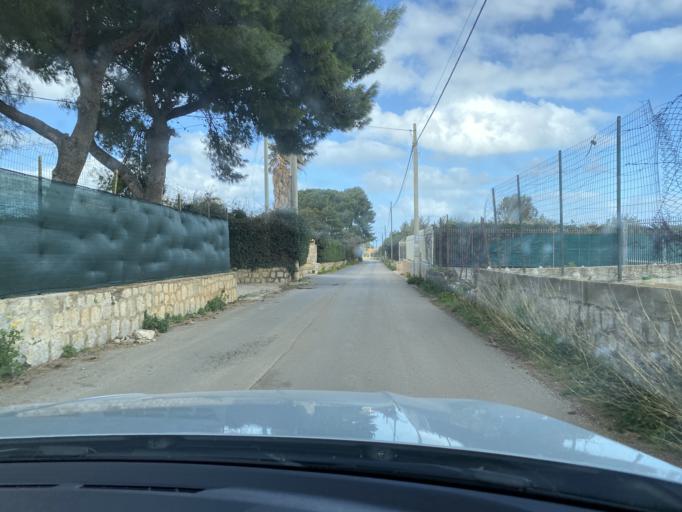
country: IT
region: Sicily
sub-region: Palermo
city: Carini
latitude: 38.1505
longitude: 13.1682
